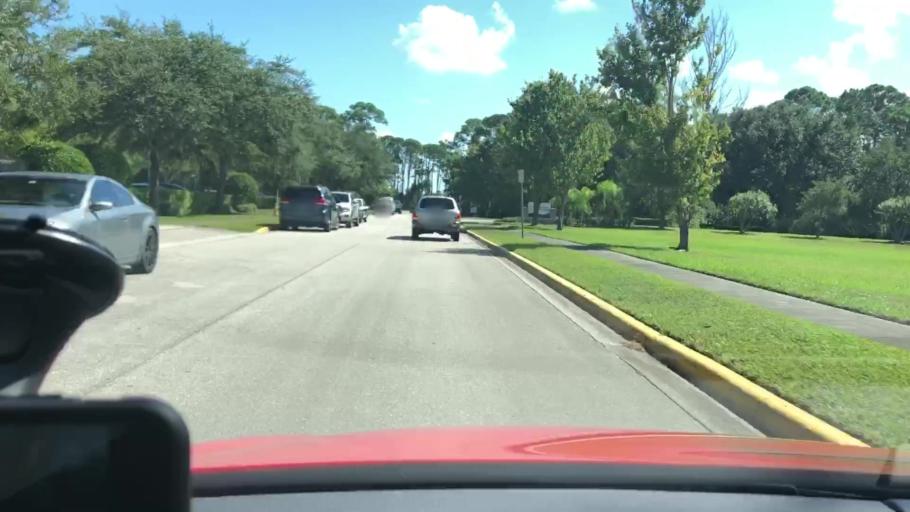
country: US
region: Florida
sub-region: Volusia County
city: Daytona Beach
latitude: 29.2061
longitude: -81.0623
